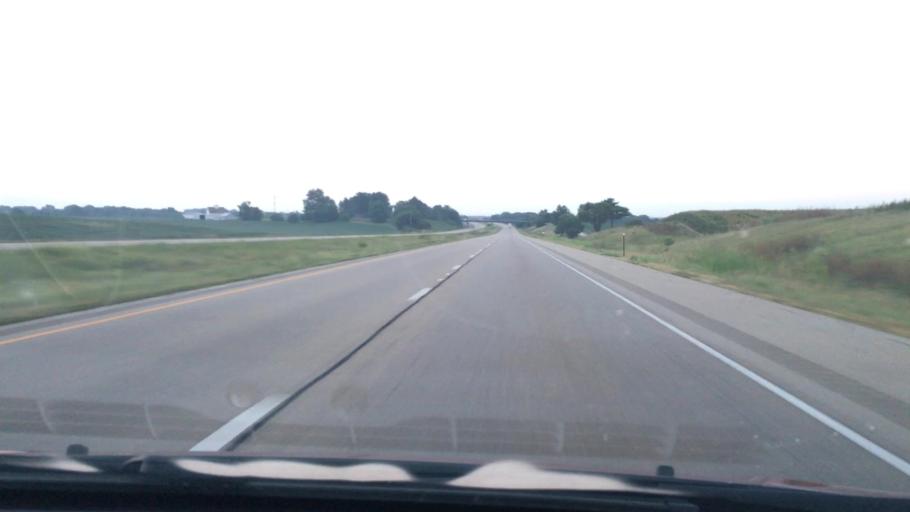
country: US
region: Illinois
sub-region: Bureau County
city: Ladd
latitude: 41.3812
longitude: -89.2657
